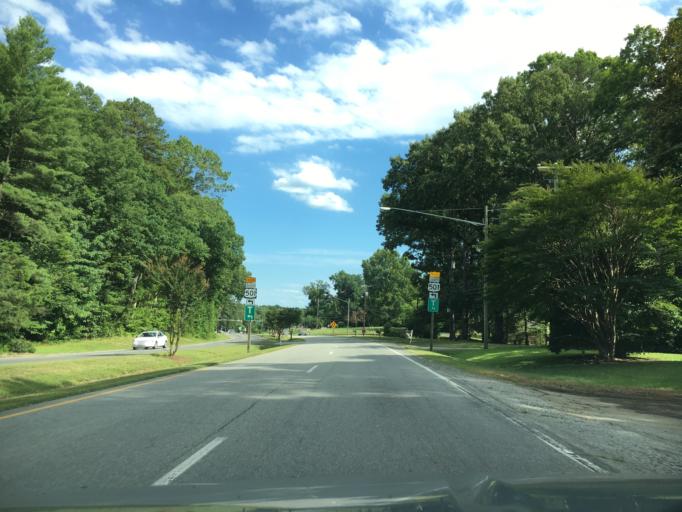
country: US
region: Virginia
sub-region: Halifax County
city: South Boston
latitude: 36.7170
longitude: -78.9163
